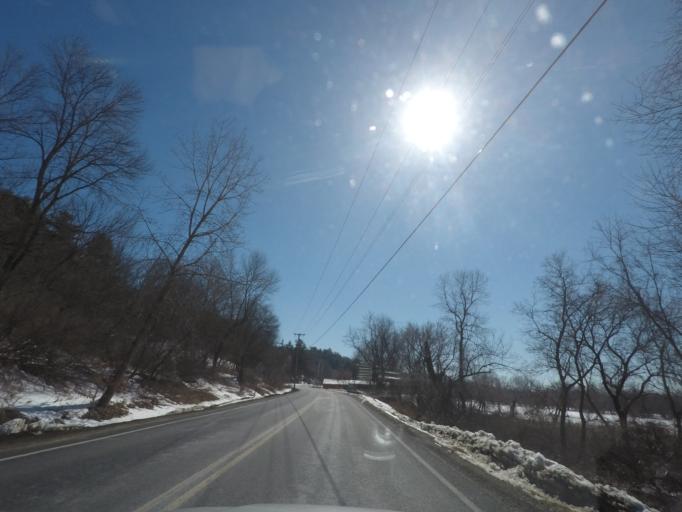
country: US
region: New York
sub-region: Saratoga County
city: Schuylerville
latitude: 43.1093
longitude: -73.5689
